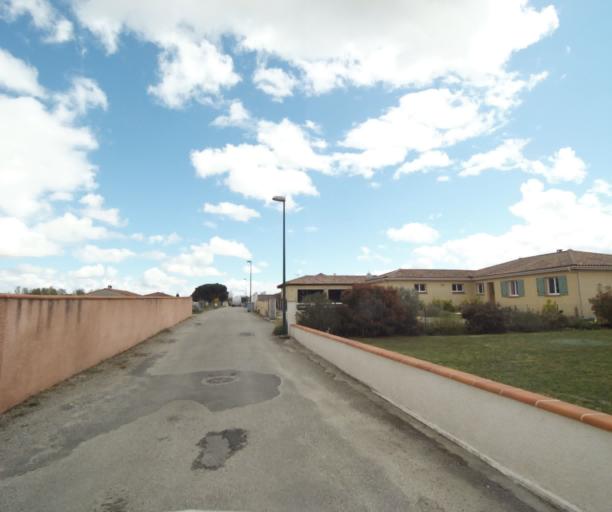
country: FR
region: Midi-Pyrenees
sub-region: Departement de l'Ariege
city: Saverdun
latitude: 43.2391
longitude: 1.5905
